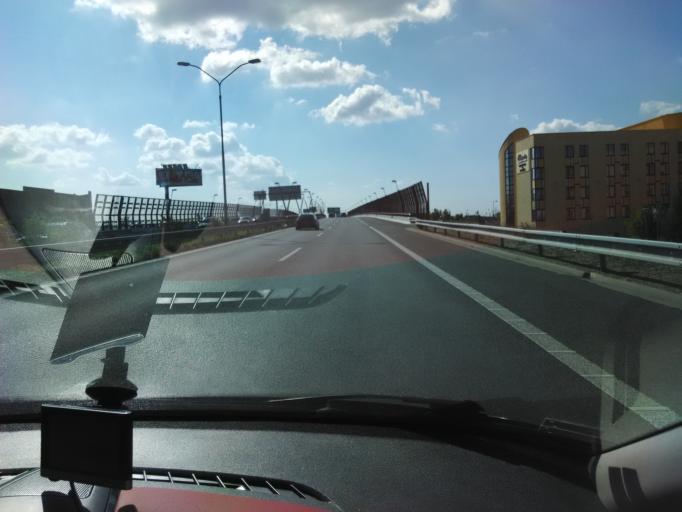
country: SK
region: Bratislavsky
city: Bratislava
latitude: 48.1631
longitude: 17.1830
